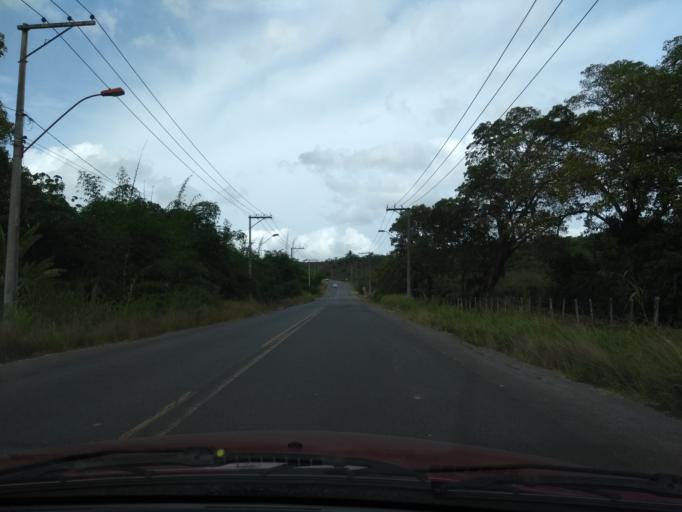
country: BR
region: Bahia
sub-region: Sao Francisco Do Conde
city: Sao Francisco do Conde
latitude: -12.6103
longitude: -38.6500
